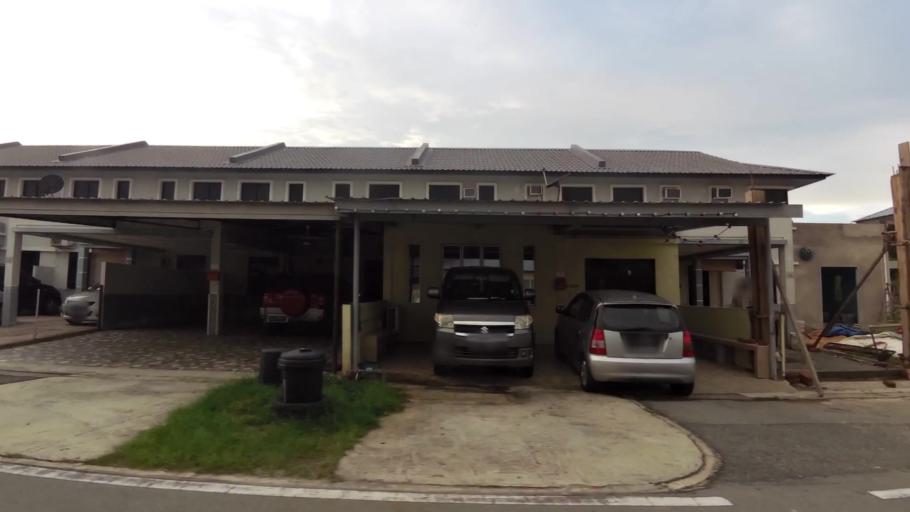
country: BN
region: Brunei and Muara
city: Bandar Seri Begawan
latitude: 4.9980
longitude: 114.9887
